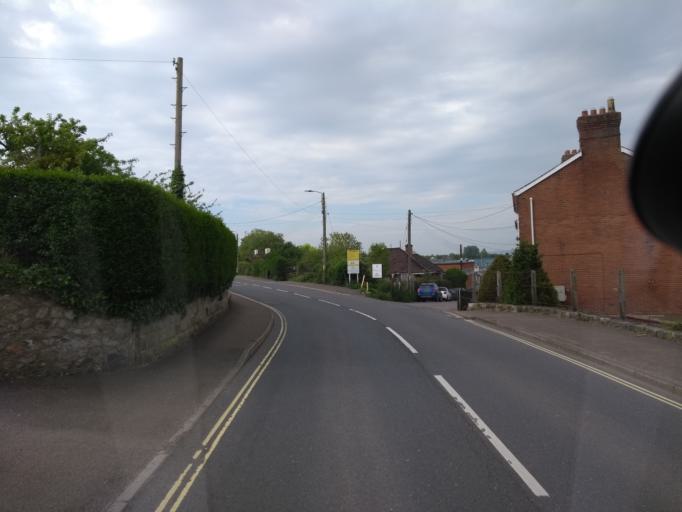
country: GB
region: England
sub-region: Devon
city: Axminster
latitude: 50.7792
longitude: -3.0029
